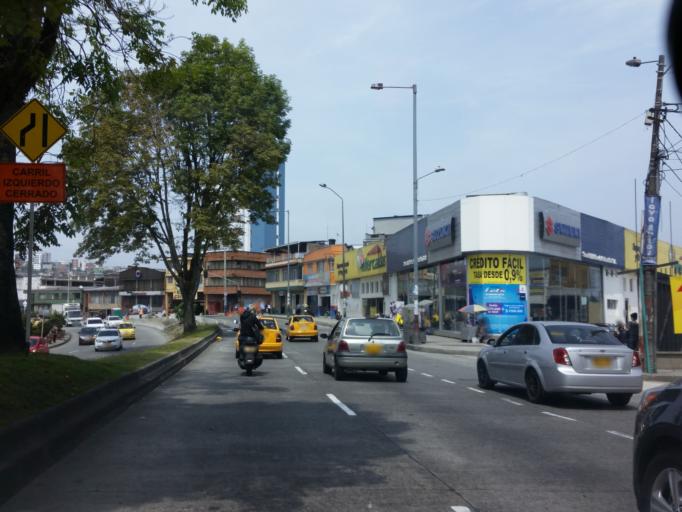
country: CO
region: Caldas
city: Manizales
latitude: 5.0698
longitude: -75.5131
